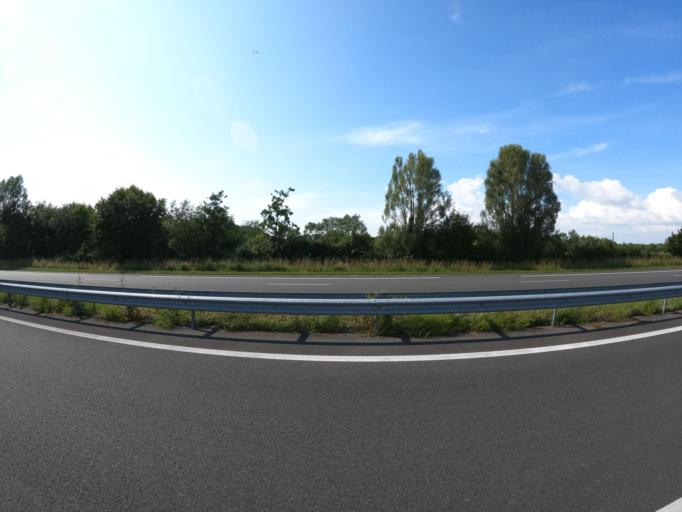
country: FR
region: Pays de la Loire
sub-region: Departement de la Loire-Atlantique
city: Saint-Lumine-de-Coutais
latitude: 47.0179
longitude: -1.6950
